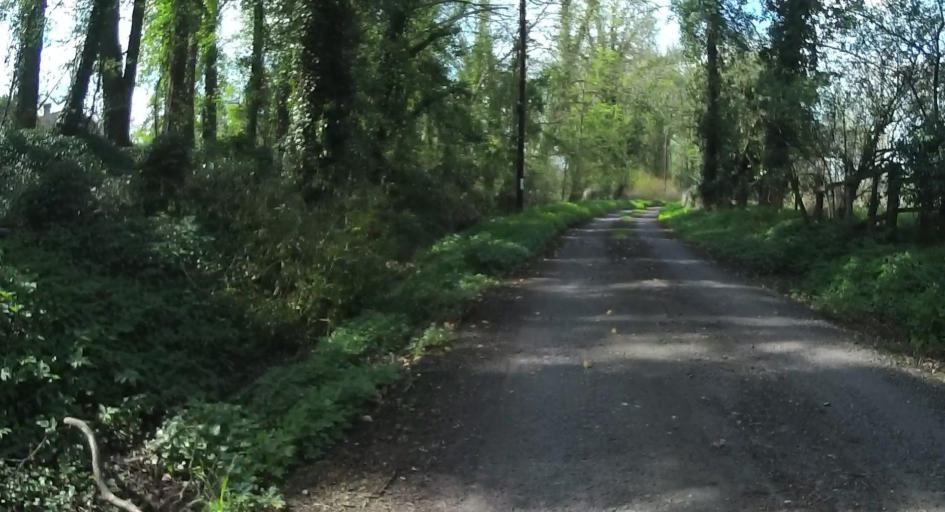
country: GB
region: England
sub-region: Hampshire
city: Andover
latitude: 51.1622
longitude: -1.4143
